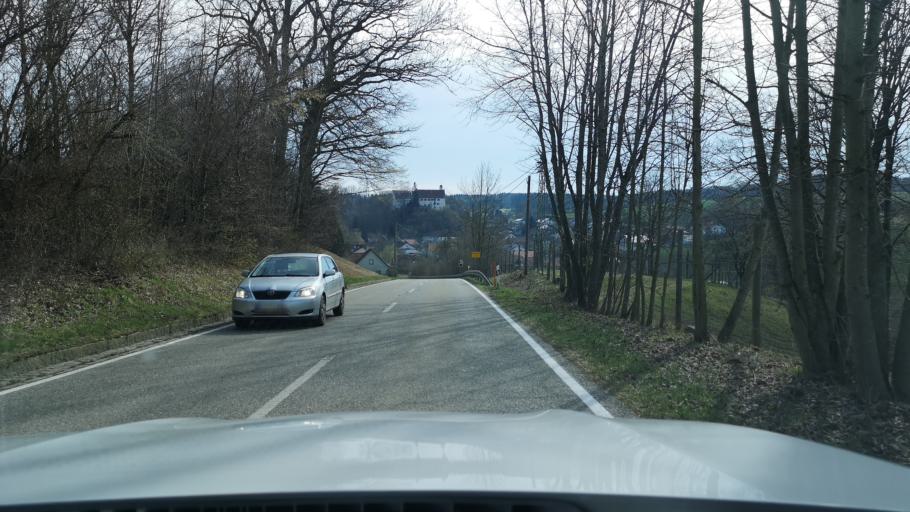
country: DE
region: Bavaria
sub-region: Upper Bavaria
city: Isen
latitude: 48.1938
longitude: 12.0503
